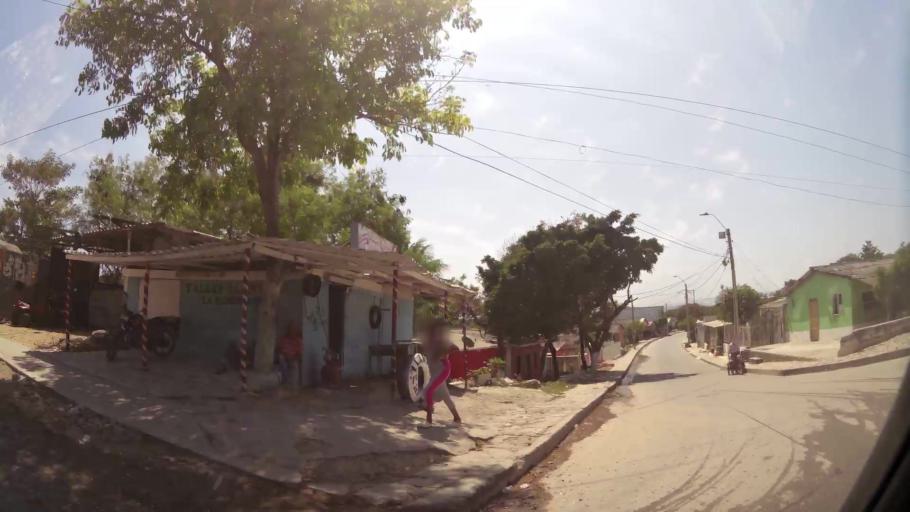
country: CO
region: Atlantico
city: Barranquilla
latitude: 10.9640
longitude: -74.8135
